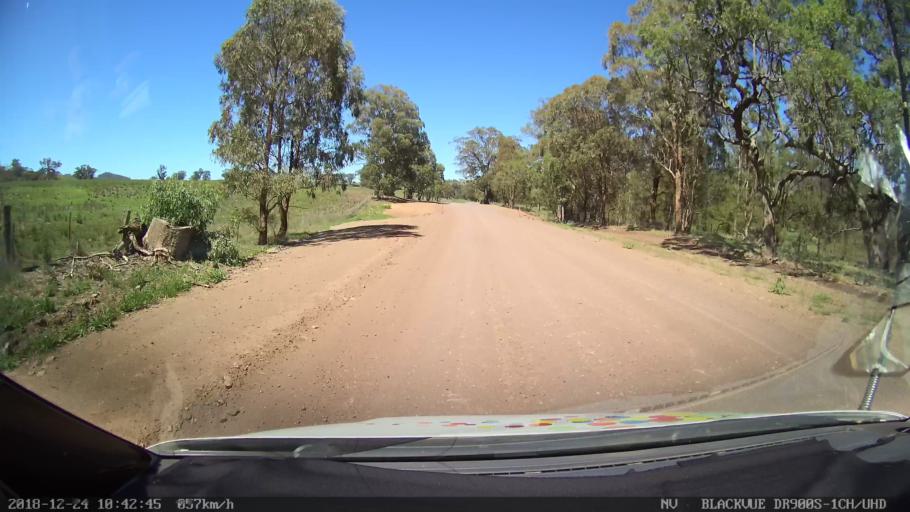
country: AU
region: New South Wales
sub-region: Upper Hunter Shire
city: Merriwa
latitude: -31.8783
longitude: 150.4510
